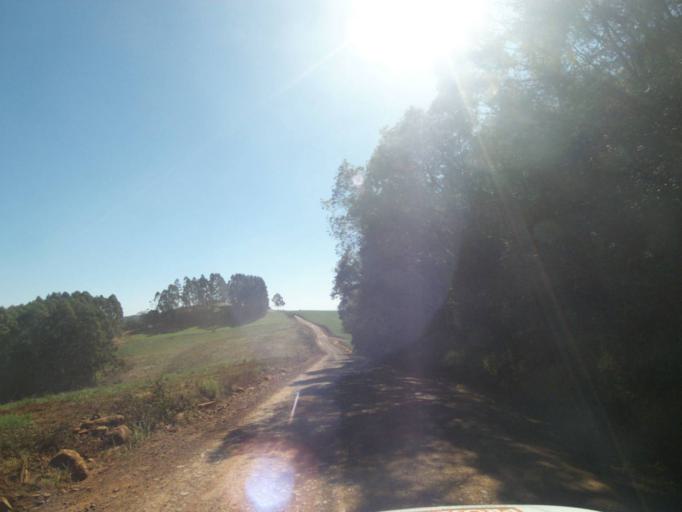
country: BR
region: Parana
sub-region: Tibagi
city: Tibagi
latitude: -24.5907
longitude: -50.6058
